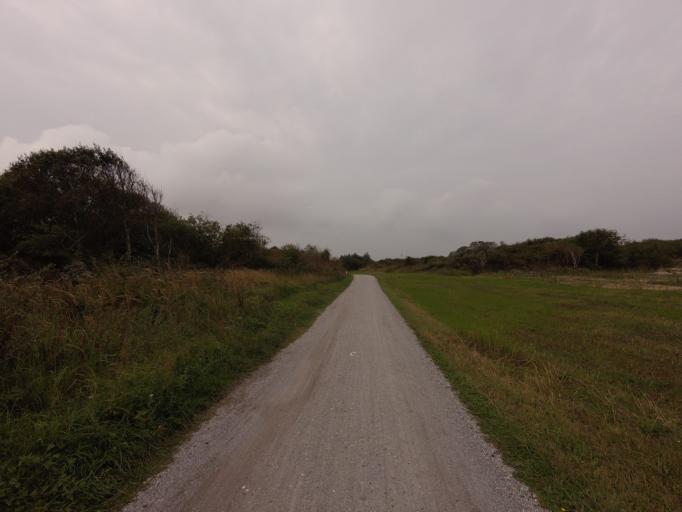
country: NL
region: Friesland
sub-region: Gemeente Schiermonnikoog
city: Schiermonnikoog
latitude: 53.4958
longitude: 6.1909
